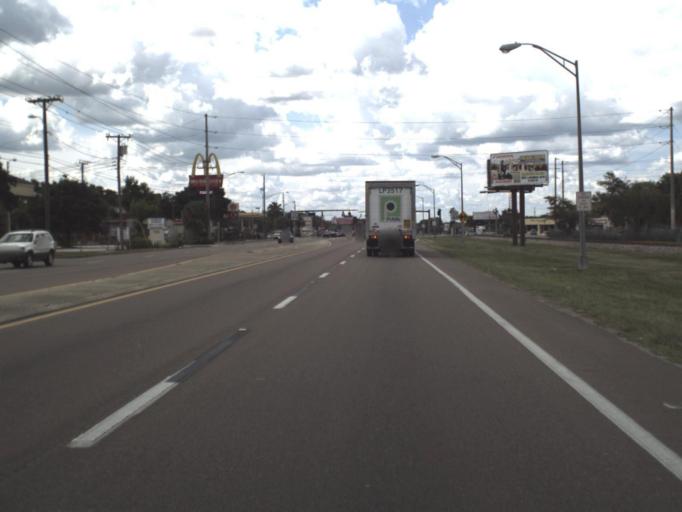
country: US
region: Florida
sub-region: Polk County
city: Crystal Lake
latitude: 28.0223
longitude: -81.9229
